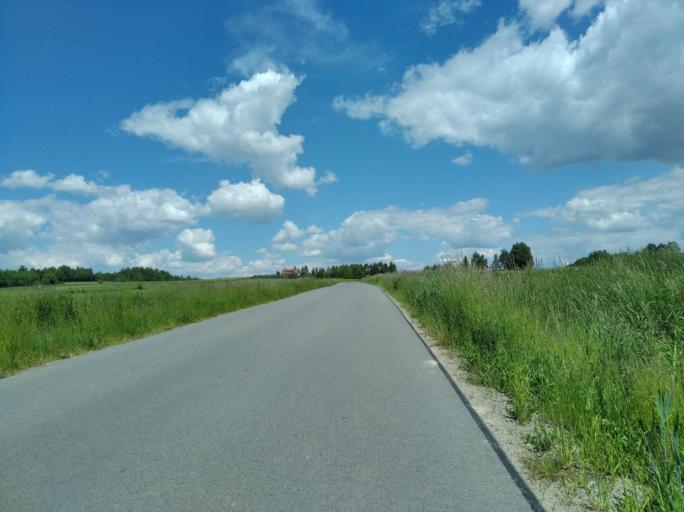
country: PL
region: Subcarpathian Voivodeship
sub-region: Powiat jasielski
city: Tarnowiec
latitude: 49.7725
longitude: 21.6114
